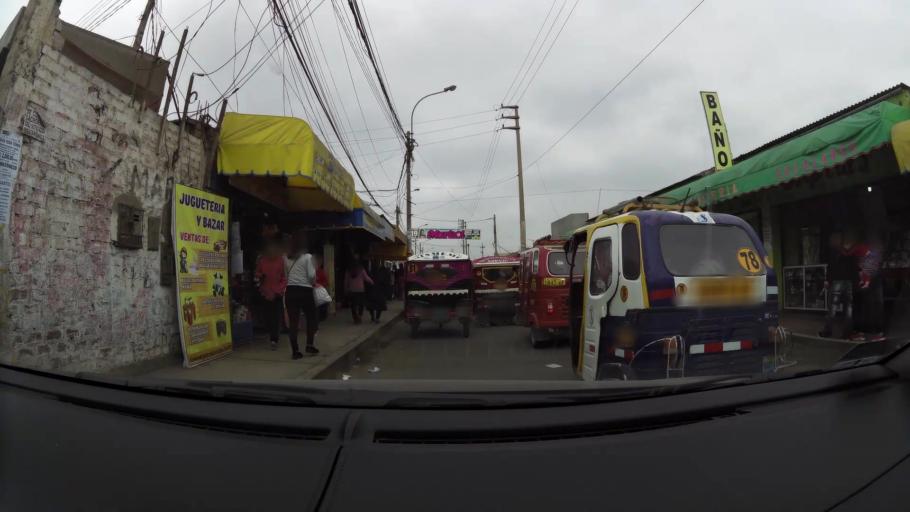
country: PE
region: Lima
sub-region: Provincia de Huaral
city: Huaral
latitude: -11.5016
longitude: -77.2061
